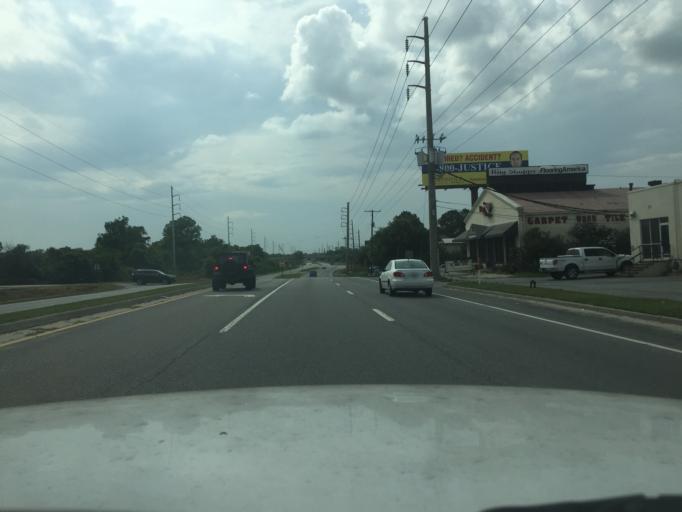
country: US
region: Georgia
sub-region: Chatham County
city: Savannah
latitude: 32.0713
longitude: -81.0636
